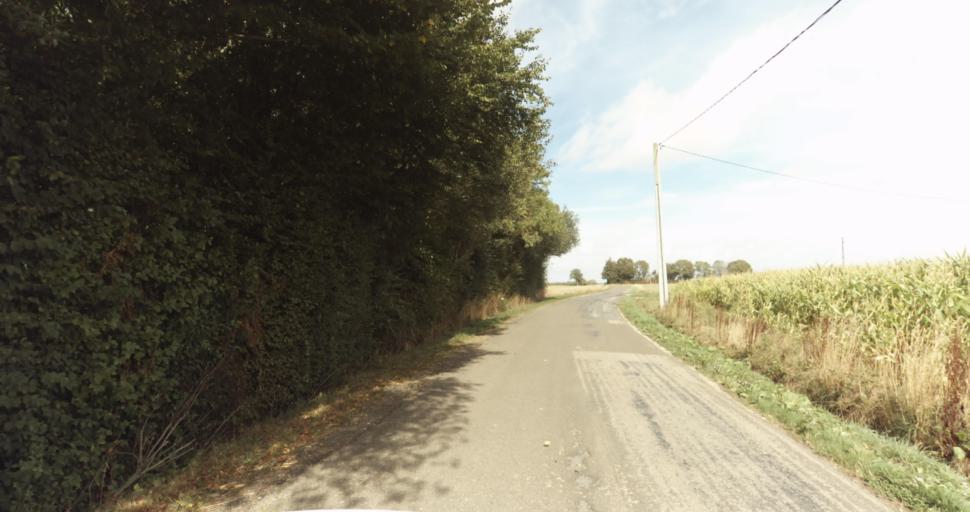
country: FR
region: Lower Normandy
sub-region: Departement de l'Orne
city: Gace
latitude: 48.8131
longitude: 0.3860
